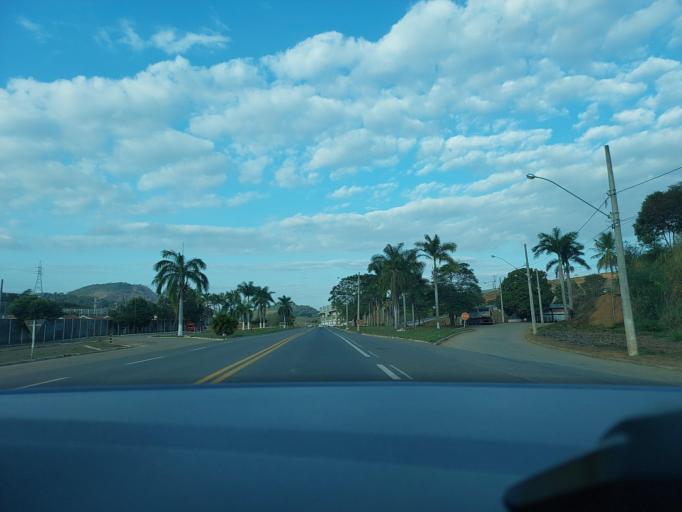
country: BR
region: Minas Gerais
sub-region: Muriae
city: Muriae
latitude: -21.1269
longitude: -42.3427
